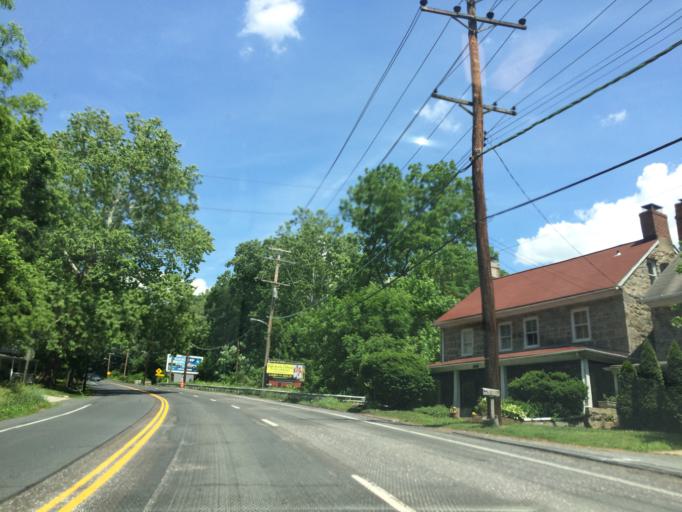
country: US
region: Maryland
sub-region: Howard County
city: Ellicott City
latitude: 39.2625
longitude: -76.7825
